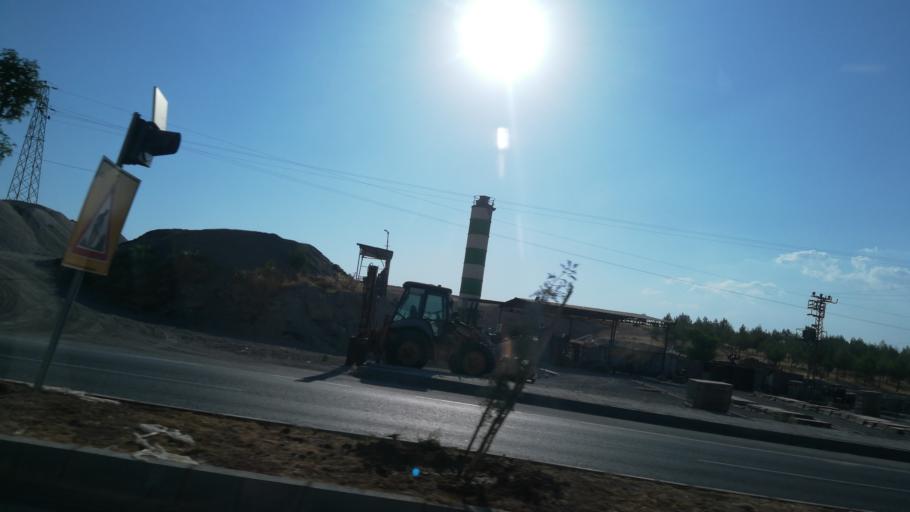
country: TR
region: Mardin
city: Midyat
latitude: 37.4031
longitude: 41.3435
